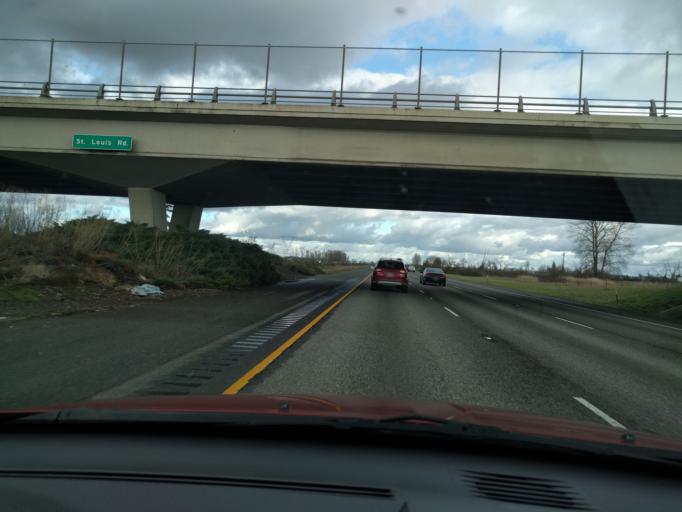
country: US
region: Oregon
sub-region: Marion County
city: Gervais
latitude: 45.1149
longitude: -122.9174
